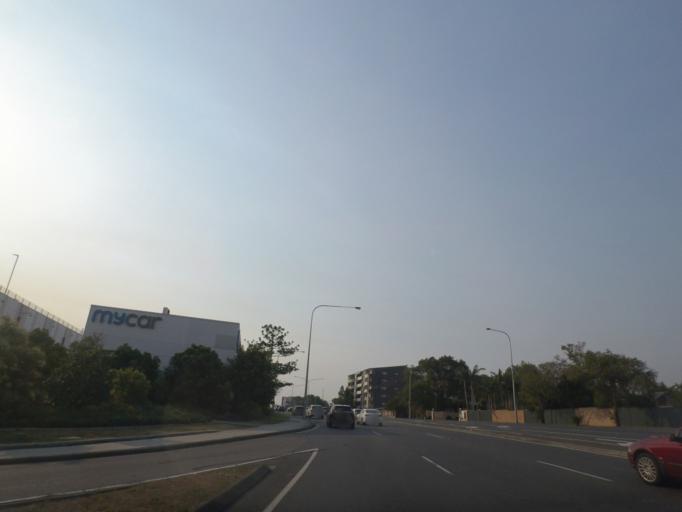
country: AU
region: Queensland
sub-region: Brisbane
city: Upper Mount Gravatt
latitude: -27.5639
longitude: 153.0867
